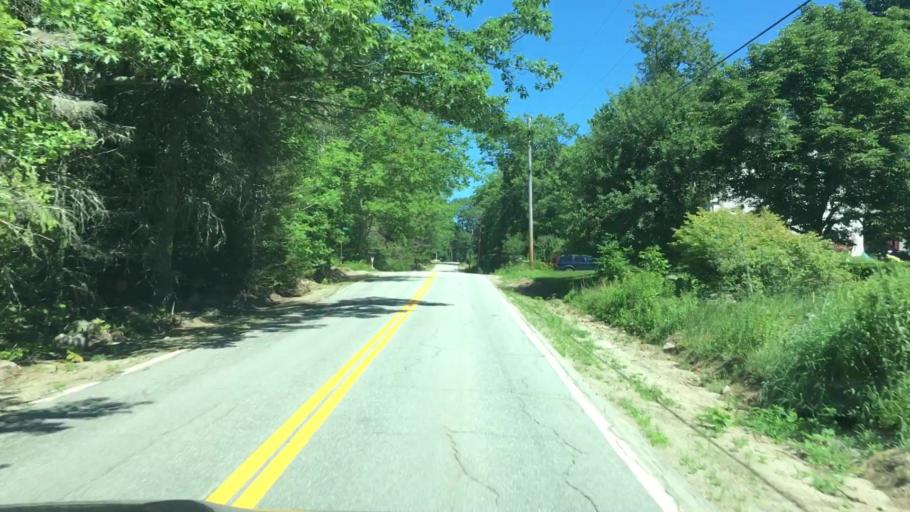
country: US
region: Maine
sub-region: Hancock County
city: Penobscot
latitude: 44.4296
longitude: -68.7134
